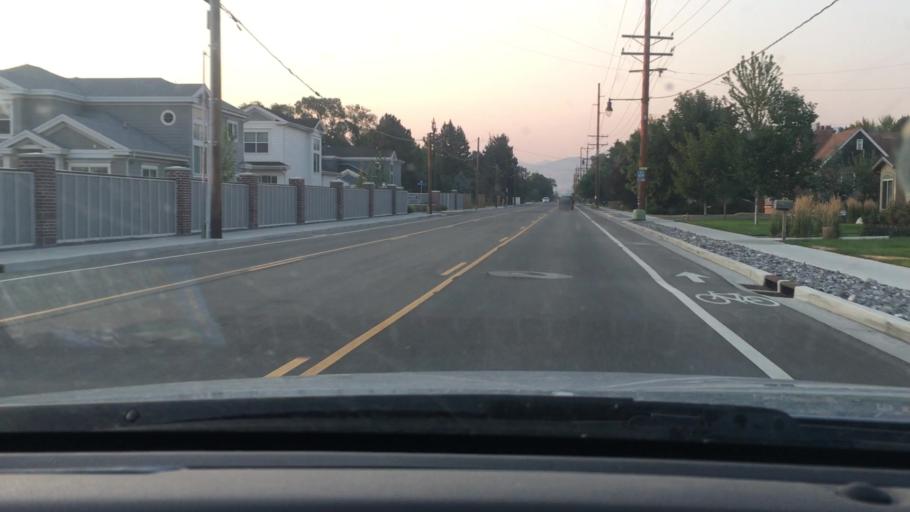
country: US
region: Utah
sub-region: Salt Lake County
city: Canyon Rim
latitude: 40.6909
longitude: -111.8244
